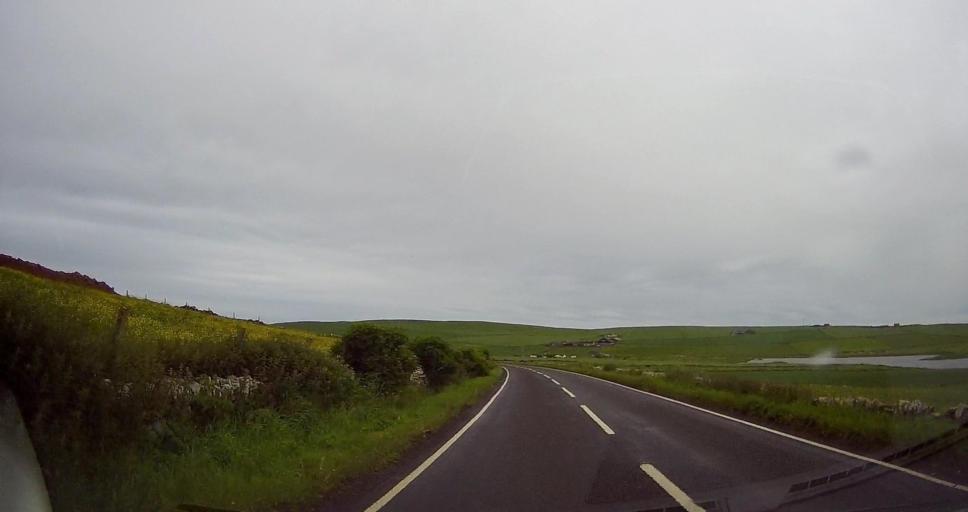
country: GB
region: Scotland
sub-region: Orkney Islands
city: Stromness
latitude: 59.0100
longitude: -3.2954
